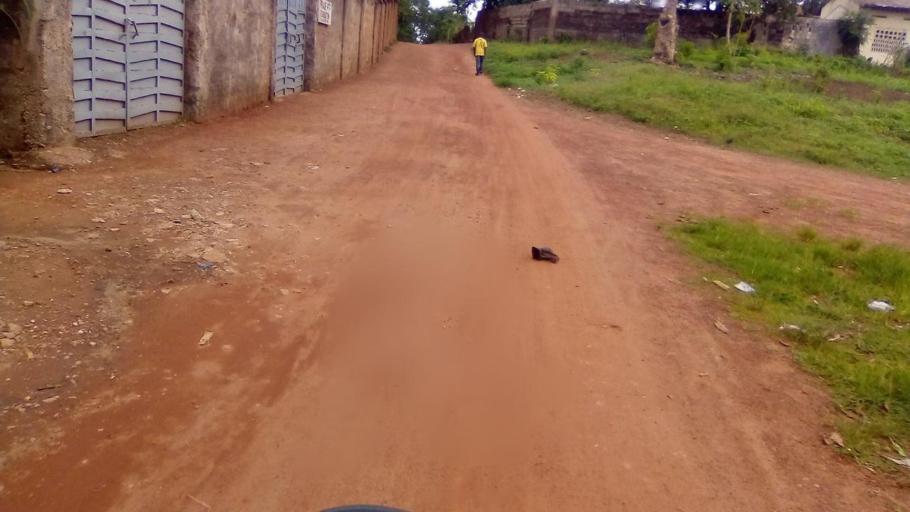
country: SL
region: Southern Province
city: Bo
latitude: 7.9590
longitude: -11.7261
